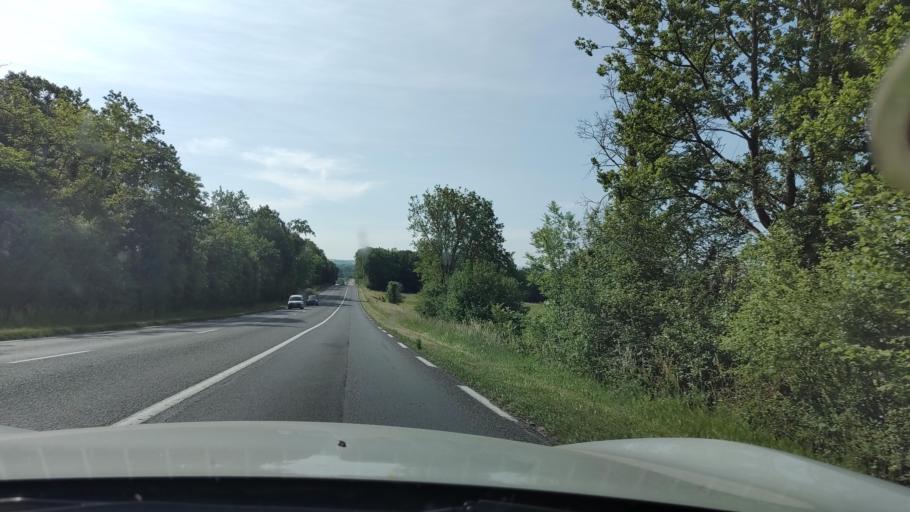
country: FR
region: Ile-de-France
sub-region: Departement de Seine-et-Marne
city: Sourdun
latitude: 48.5217
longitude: 3.4143
